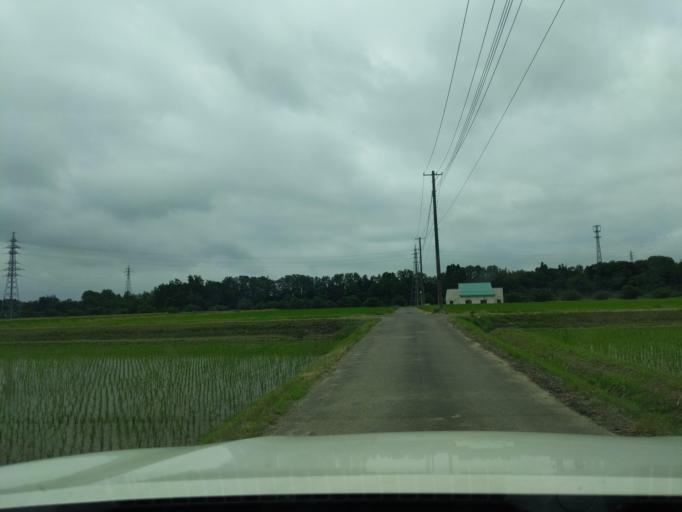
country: JP
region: Fukushima
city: Koriyama
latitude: 37.4541
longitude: 140.3240
